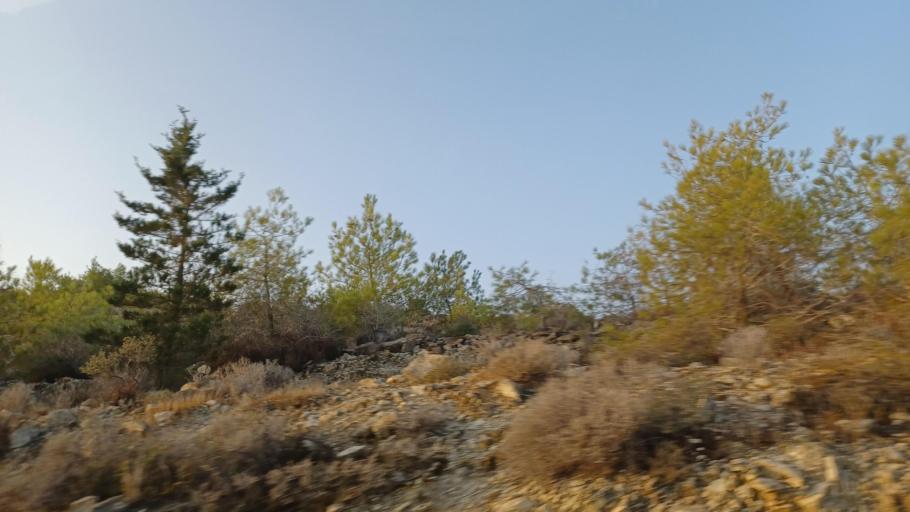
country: CY
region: Lefkosia
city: Lympia
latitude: 34.9979
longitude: 33.5238
